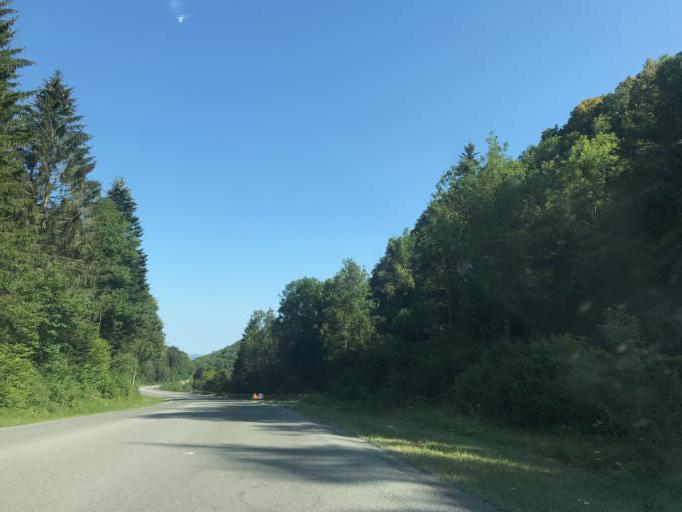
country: FR
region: Franche-Comte
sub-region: Departement du Jura
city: Lavans-les-Saint-Claude
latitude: 46.3892
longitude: 5.7427
